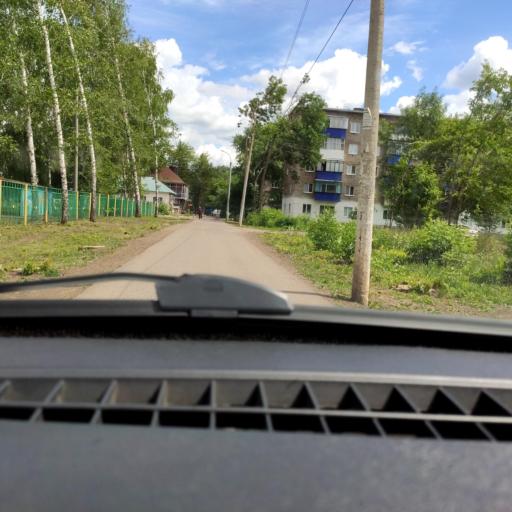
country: RU
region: Bashkortostan
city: Sterlitamak
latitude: 53.6357
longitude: 55.9311
